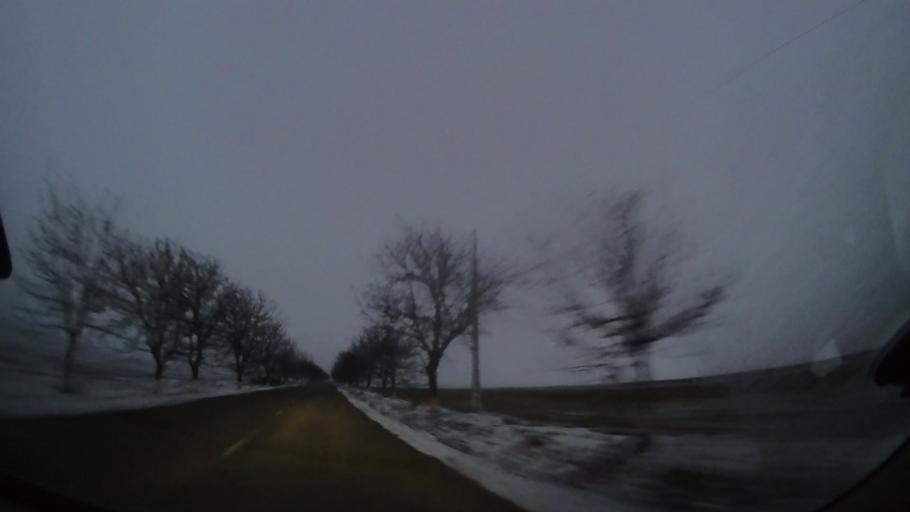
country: RO
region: Vaslui
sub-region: Comuna Dimitrie Cantemir
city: Dimitrie Cantemir
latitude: 46.5084
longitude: 28.0486
